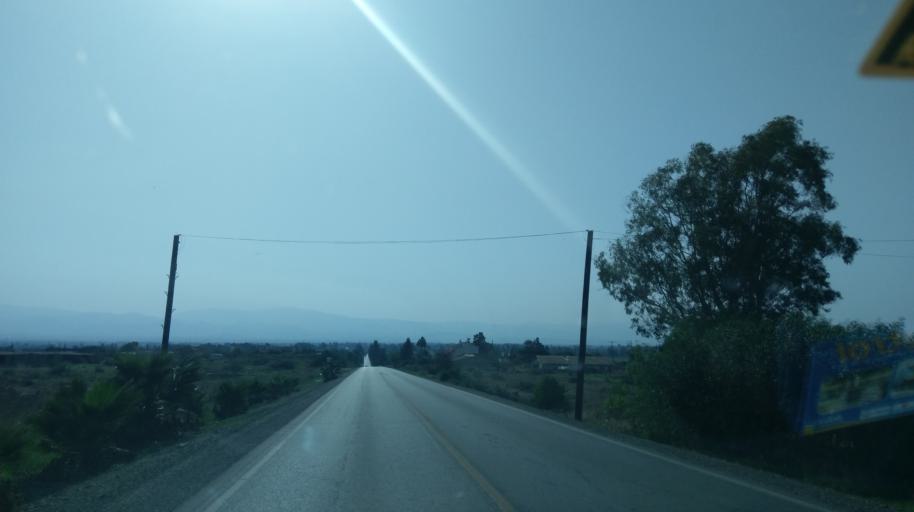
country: CY
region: Lefkosia
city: Morfou
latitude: 35.2284
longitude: 33.0132
